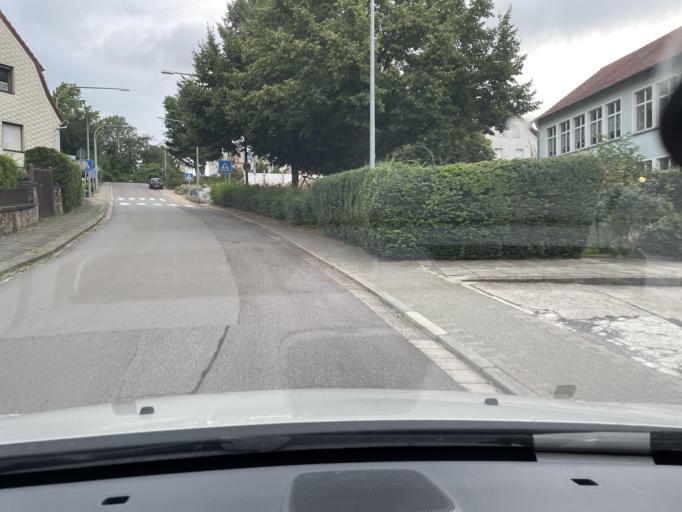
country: DE
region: Saarland
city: Sulzbach
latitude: 49.2836
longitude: 7.0704
